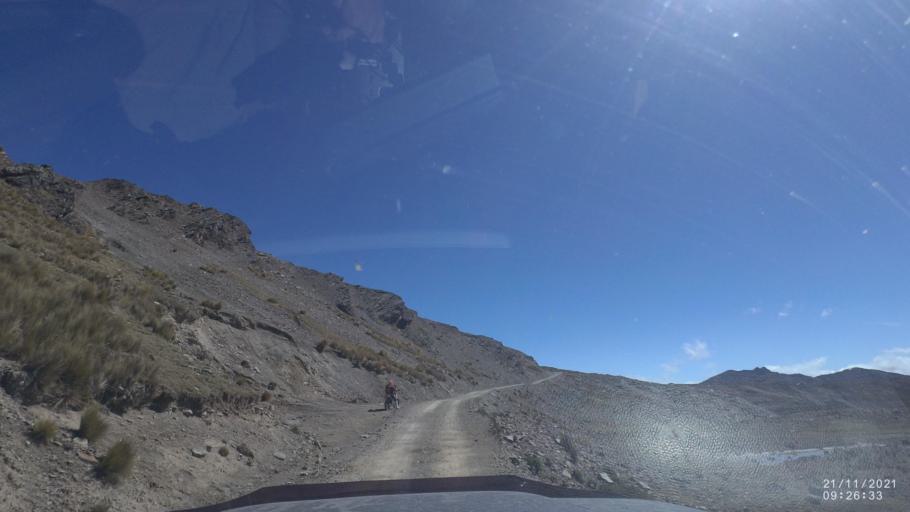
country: BO
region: Cochabamba
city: Cochabamba
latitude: -17.0865
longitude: -66.2539
